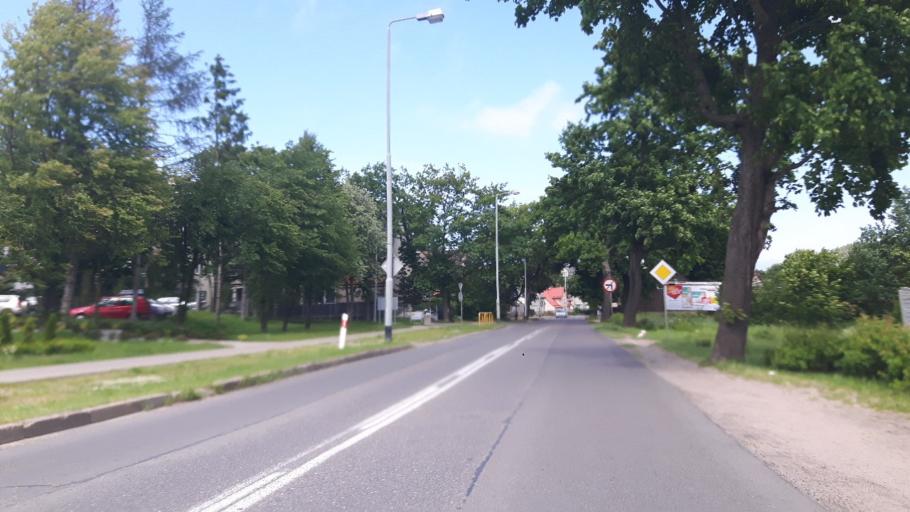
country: PL
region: Pomeranian Voivodeship
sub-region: Powiat slupski
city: Ustka
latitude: 54.5755
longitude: 16.8530
